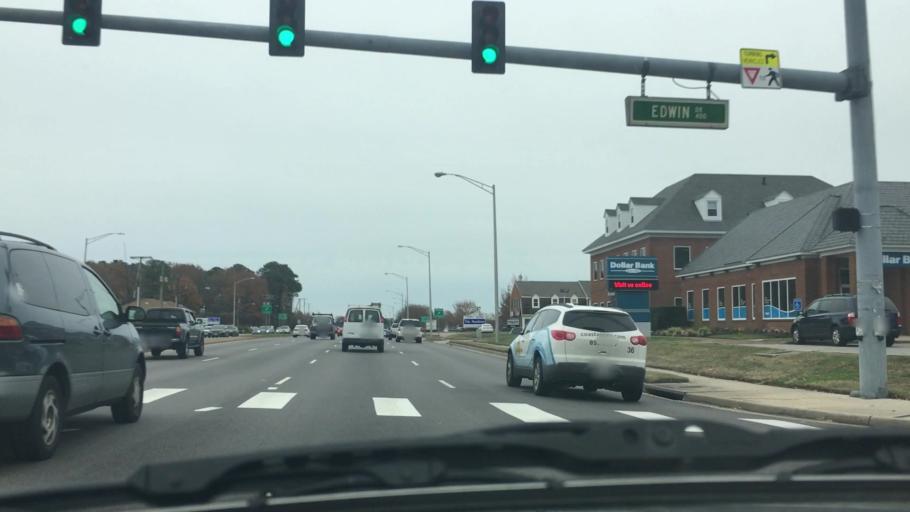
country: US
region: Virginia
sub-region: City of Chesapeake
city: Chesapeake
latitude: 36.8261
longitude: -76.1309
